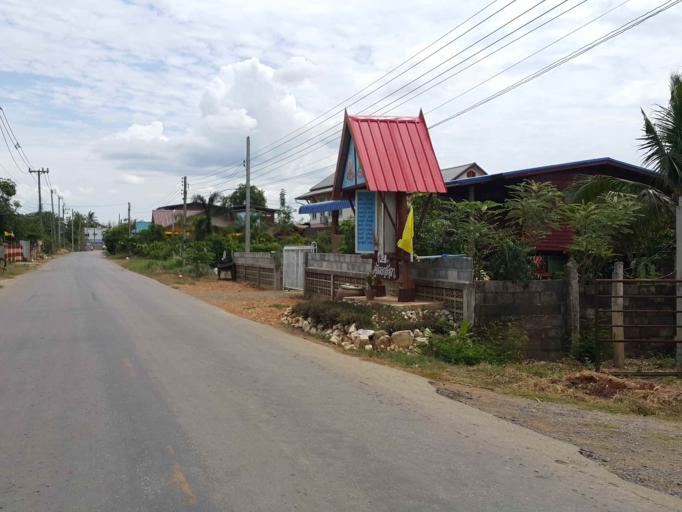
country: TH
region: Sukhothai
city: Thung Saliam
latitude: 17.3255
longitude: 99.5496
